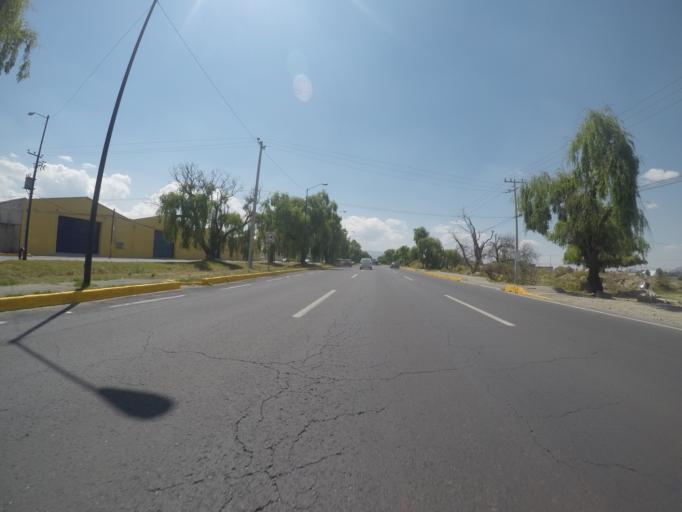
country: MX
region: Mexico
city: Cacalomacan
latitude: 19.2568
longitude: -99.6980
